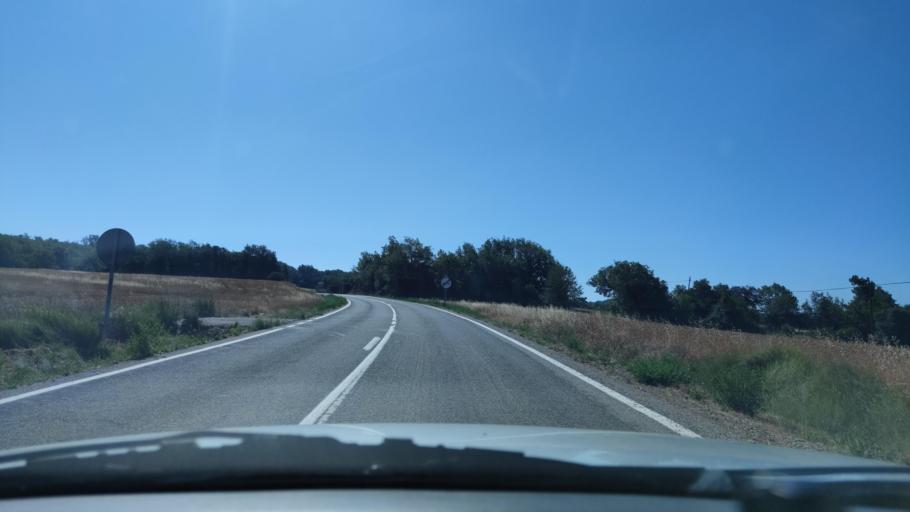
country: ES
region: Catalonia
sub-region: Provincia de Lleida
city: Solsona
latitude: 41.8966
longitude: 1.5420
